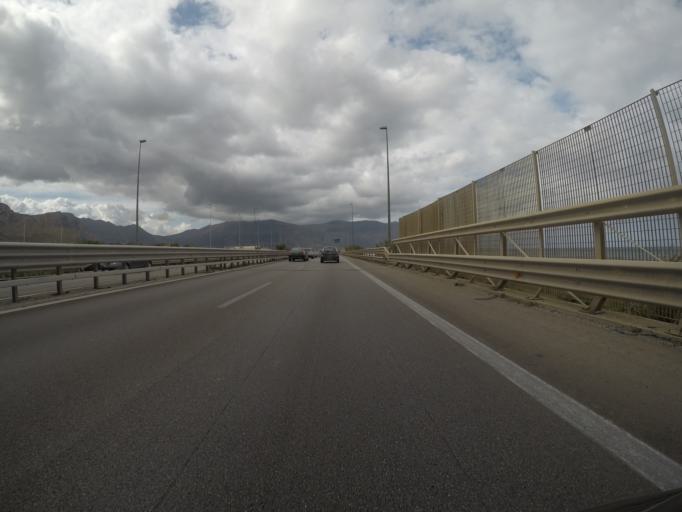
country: IT
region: Sicily
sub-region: Palermo
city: Capaci
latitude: 38.1785
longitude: 13.2248
